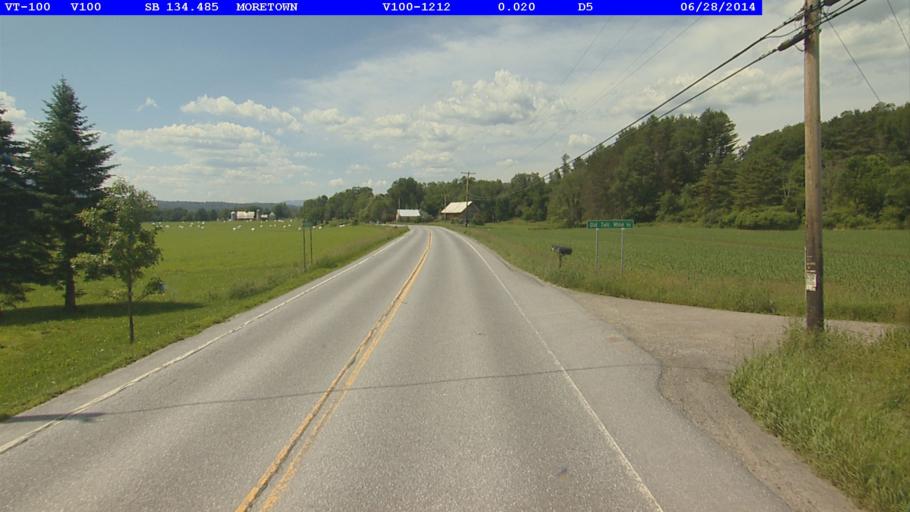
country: US
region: Vermont
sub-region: Washington County
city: Waterbury
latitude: 44.2353
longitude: -72.7800
